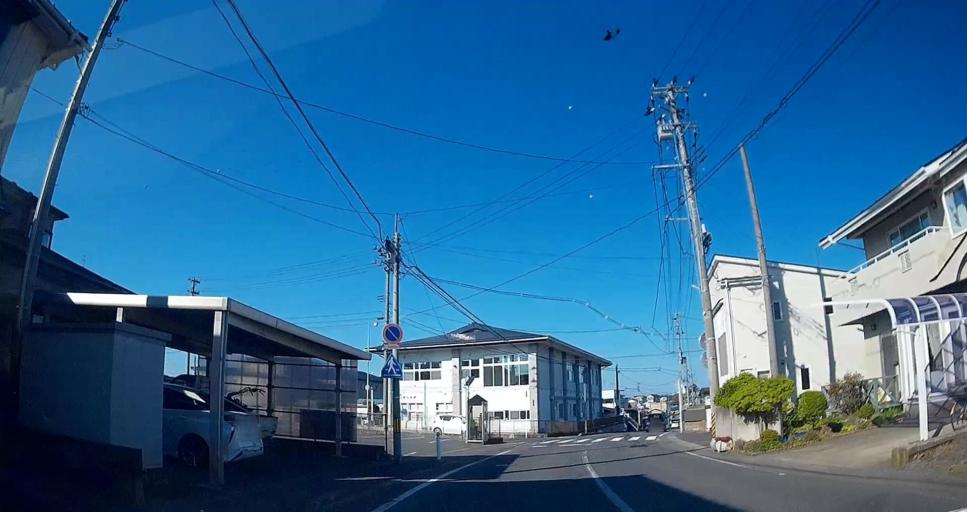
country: JP
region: Aomori
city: Hachinohe
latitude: 40.5232
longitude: 141.5464
